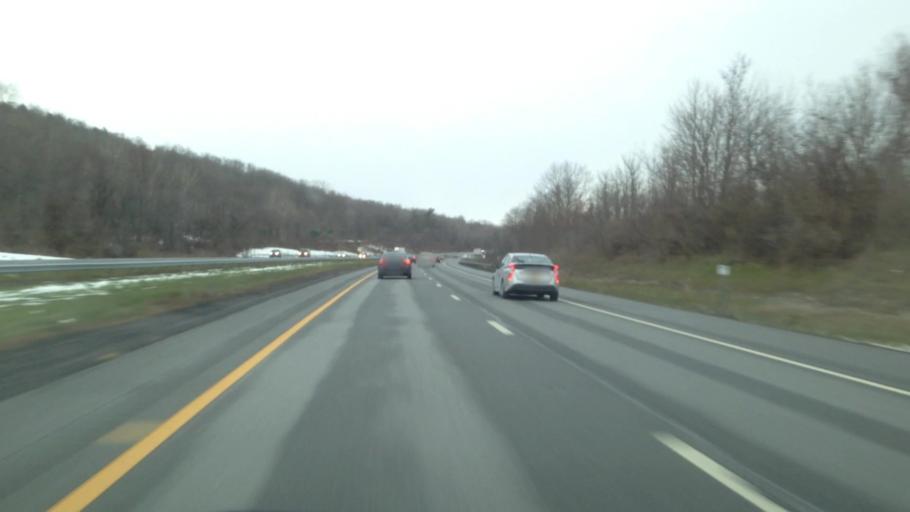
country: US
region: New York
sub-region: Montgomery County
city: Saint Johnsville
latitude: 42.9903
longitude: -74.7272
